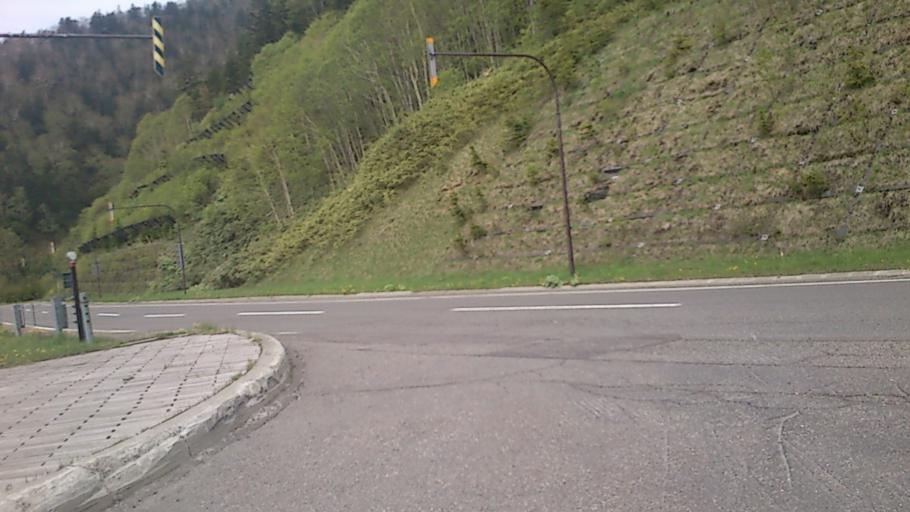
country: JP
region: Hokkaido
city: Kamikawa
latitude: 43.5792
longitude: 143.1288
